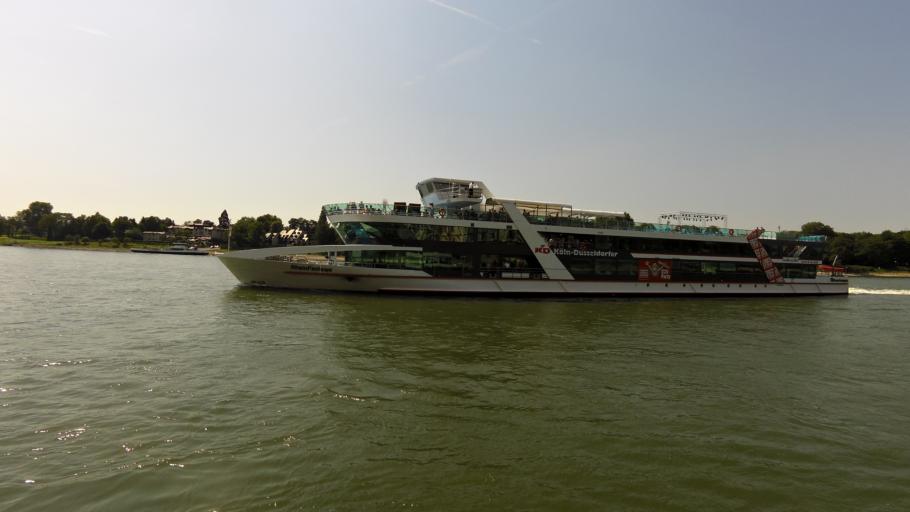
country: DE
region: North Rhine-Westphalia
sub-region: Regierungsbezirk Koln
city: Konigswinter
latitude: 50.6737
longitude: 7.1908
